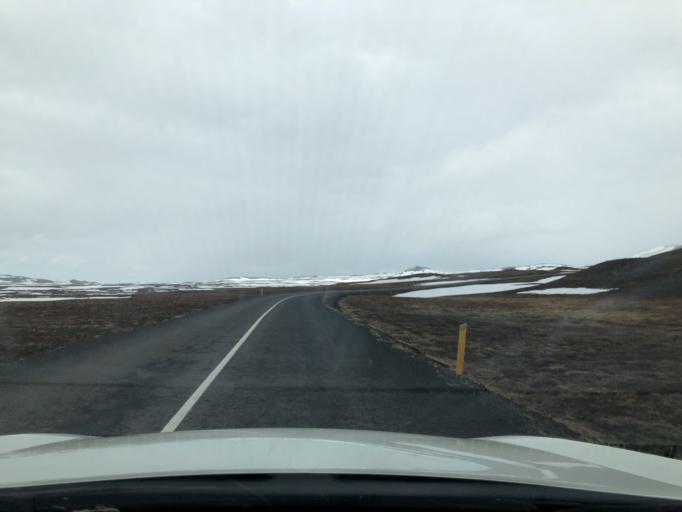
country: IS
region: Northeast
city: Laugar
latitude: 65.7151
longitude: -16.7621
